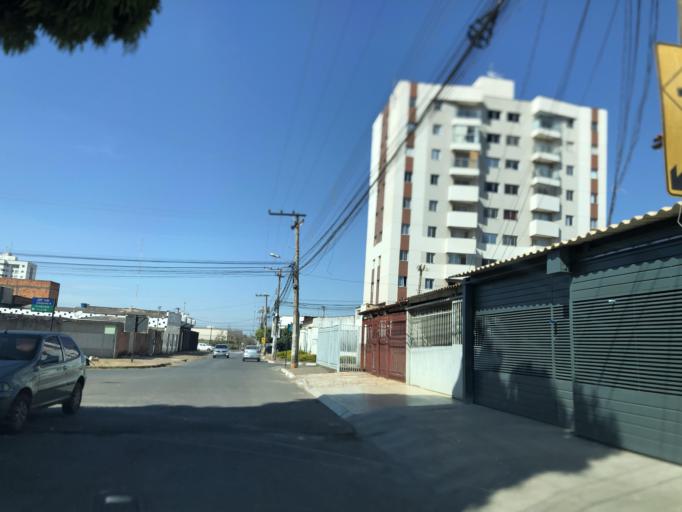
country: BR
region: Federal District
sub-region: Brasilia
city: Brasilia
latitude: -15.8733
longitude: -48.0778
